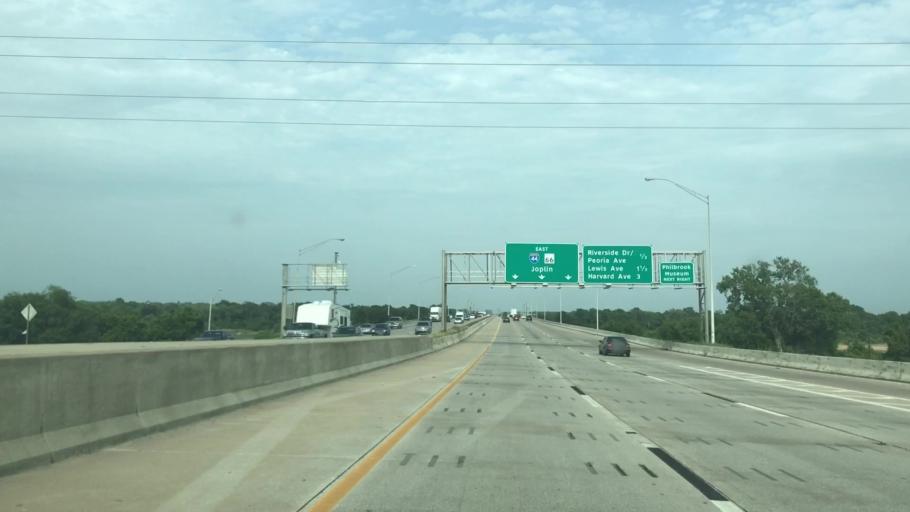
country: US
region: Oklahoma
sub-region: Tulsa County
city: Tulsa
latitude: 36.0898
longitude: -95.9937
